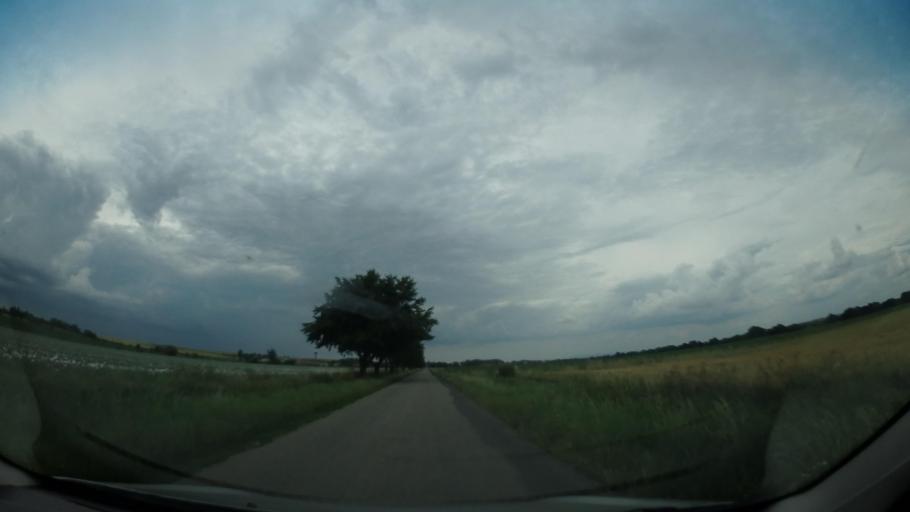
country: CZ
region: South Moravian
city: Ivanovice na Hane
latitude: 49.3219
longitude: 17.1282
